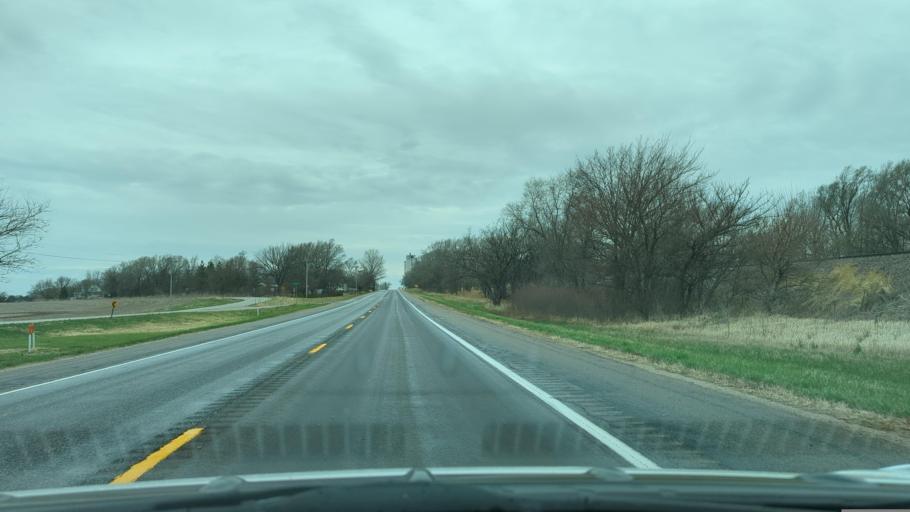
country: US
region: Nebraska
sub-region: Saunders County
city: Ashland
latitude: 40.9692
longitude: -96.4347
